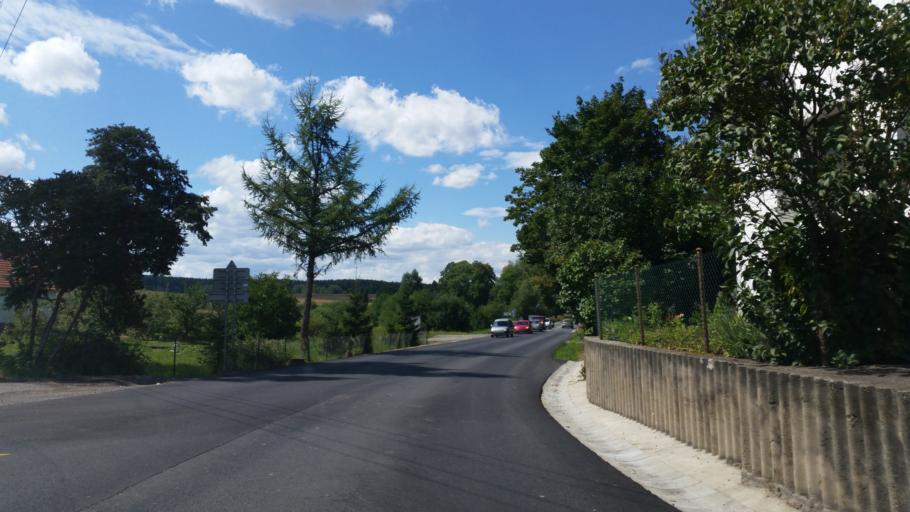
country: CZ
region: Vysocina
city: Cernovice
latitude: 49.4251
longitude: 14.9430
